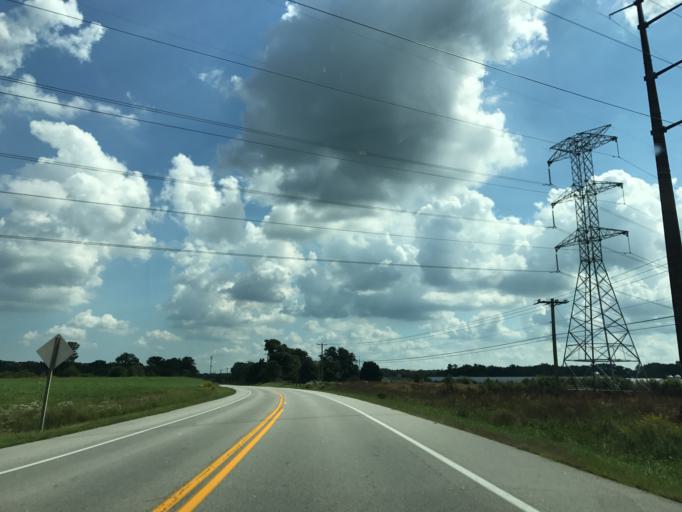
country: US
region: Maryland
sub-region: Caroline County
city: Greensboro
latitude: 39.1361
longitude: -75.8040
